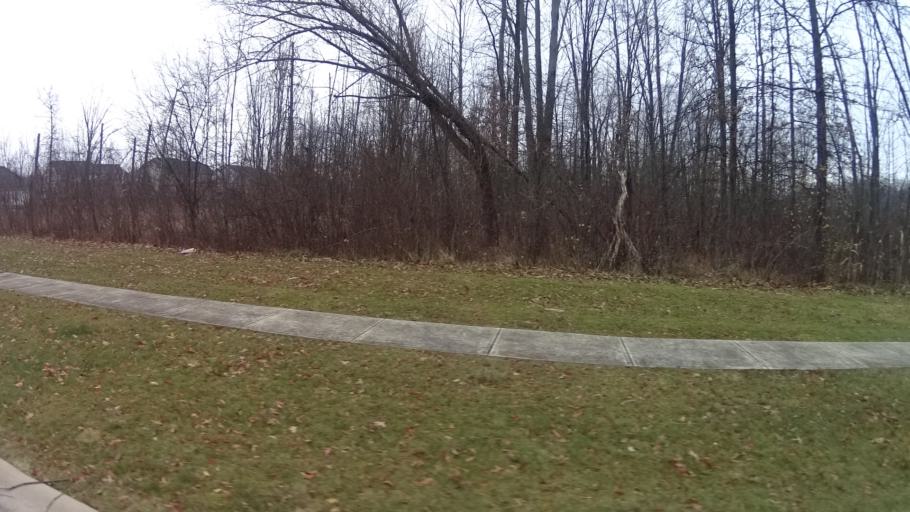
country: US
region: Ohio
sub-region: Lorain County
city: North Ridgeville
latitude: 41.3704
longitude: -81.9764
